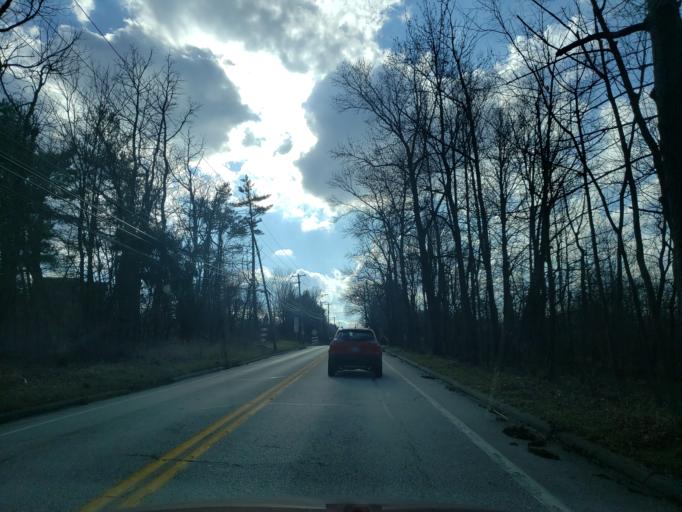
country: US
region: Pennsylvania
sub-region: Montgomery County
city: North Wales
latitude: 40.1865
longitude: -75.2700
